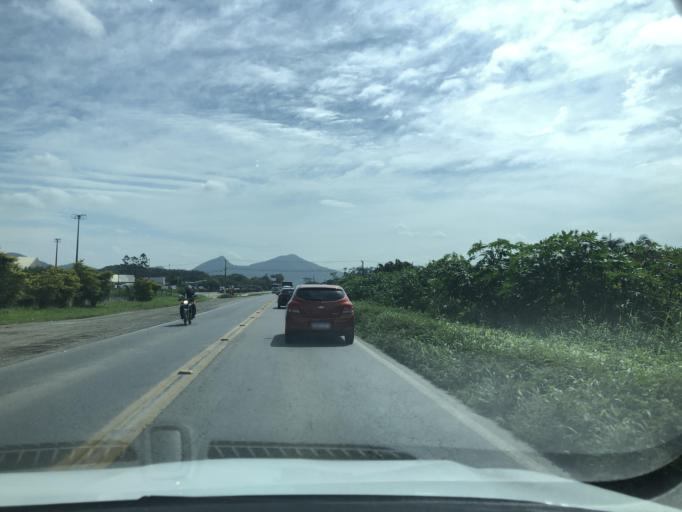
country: BR
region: Santa Catarina
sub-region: Sao Francisco Do Sul
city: Sao Francisco do Sul
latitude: -26.2620
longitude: -48.6282
